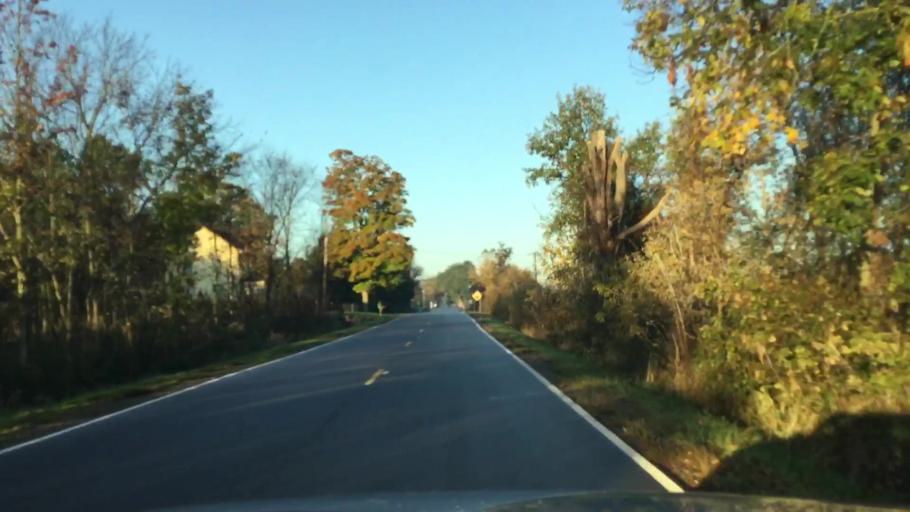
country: US
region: Michigan
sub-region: Genesee County
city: Argentine
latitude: 42.7601
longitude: -83.9364
